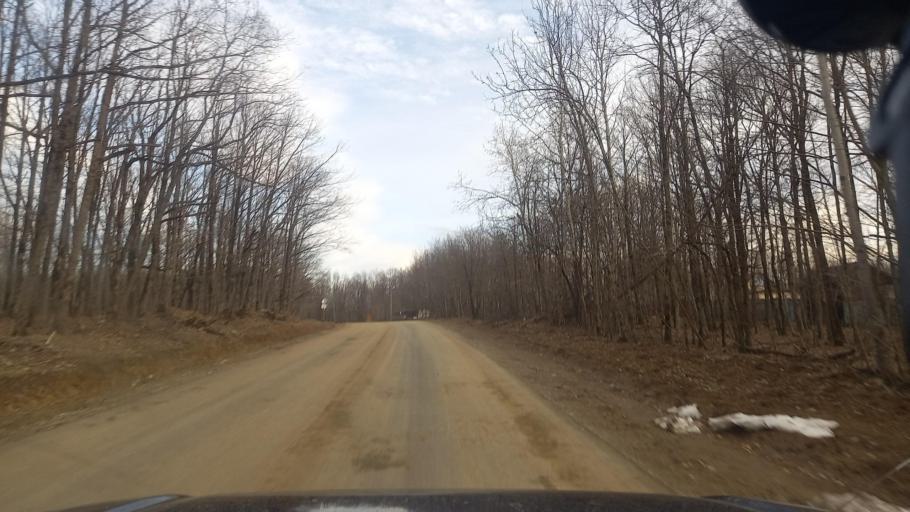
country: RU
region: Krasnodarskiy
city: Goryachiy Klyuch
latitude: 44.6996
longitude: 39.0212
